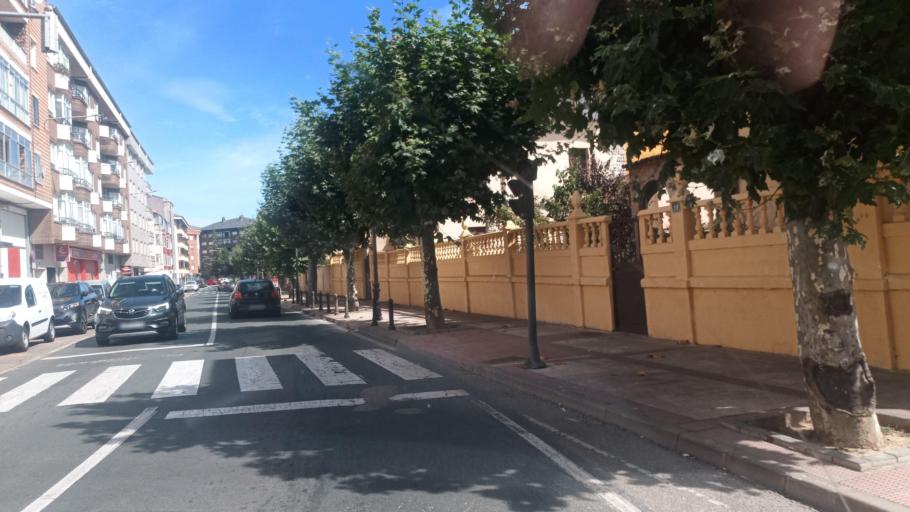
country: ES
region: Castille and Leon
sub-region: Provincia de Burgos
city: Briviesca
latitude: 42.5524
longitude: -3.3246
